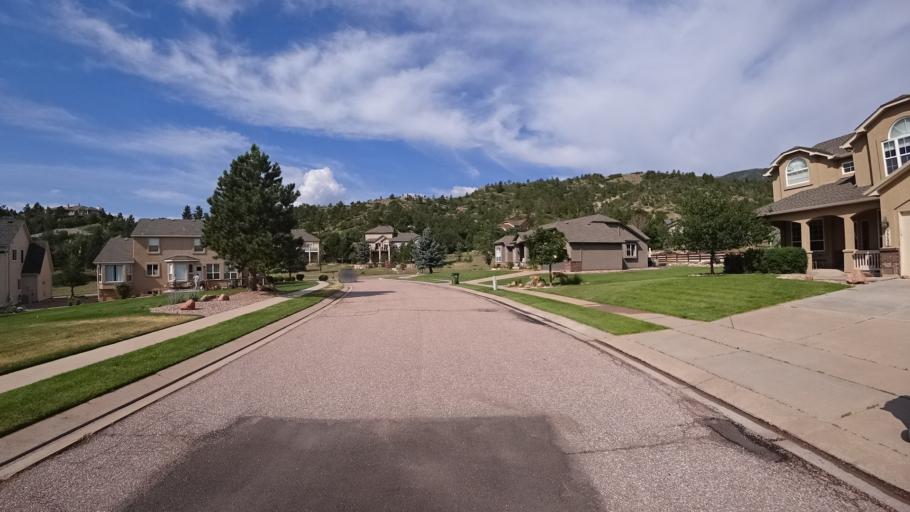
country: US
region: Colorado
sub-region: El Paso County
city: Air Force Academy
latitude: 38.9444
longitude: -104.8692
